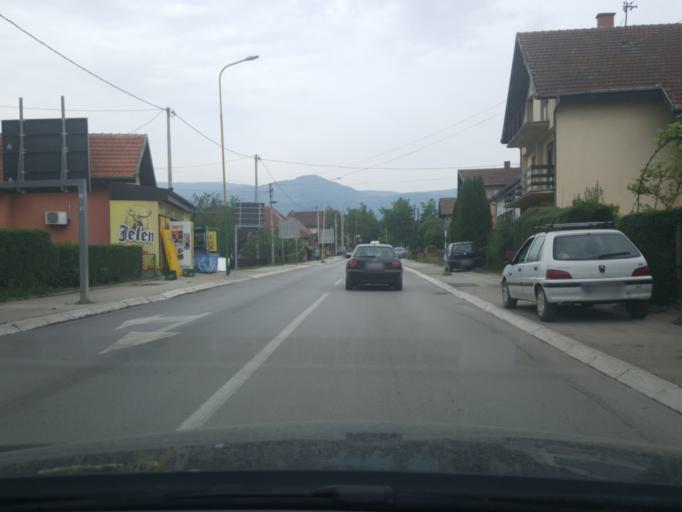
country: RS
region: Central Serbia
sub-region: Zlatiborski Okrug
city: Bajina Basta
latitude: 43.9743
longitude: 19.5692
